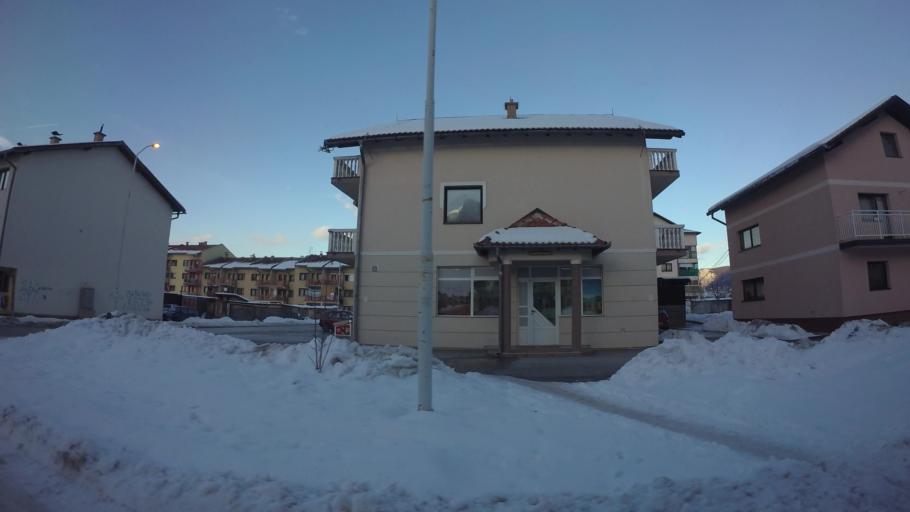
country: BA
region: Federation of Bosnia and Herzegovina
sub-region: Kanton Sarajevo
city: Sarajevo
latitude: 43.8098
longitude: 18.3617
